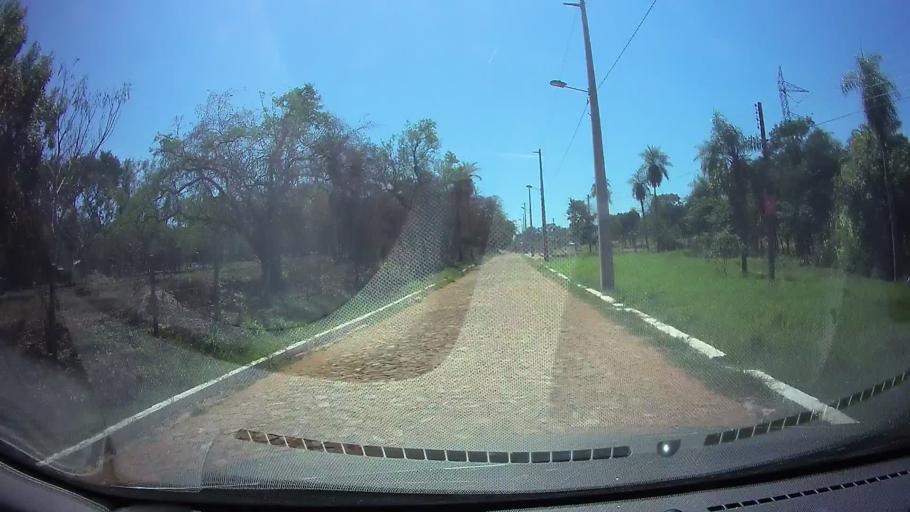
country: PY
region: Central
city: Limpio
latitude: -25.2355
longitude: -57.4387
